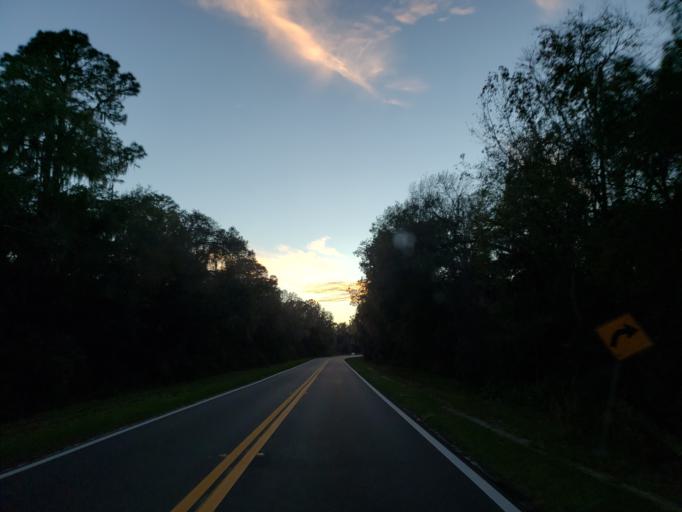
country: US
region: Florida
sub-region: Hillsborough County
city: Boyette
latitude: 27.8225
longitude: -82.2043
